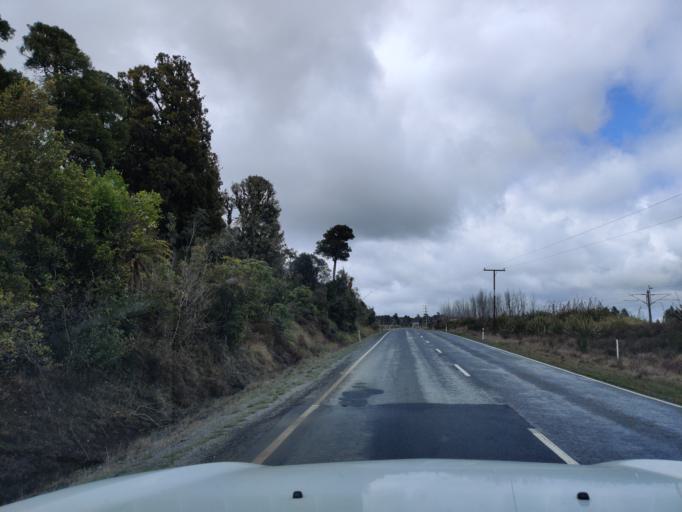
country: NZ
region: Manawatu-Wanganui
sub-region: Ruapehu District
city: Waiouru
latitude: -39.2533
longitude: 175.3880
